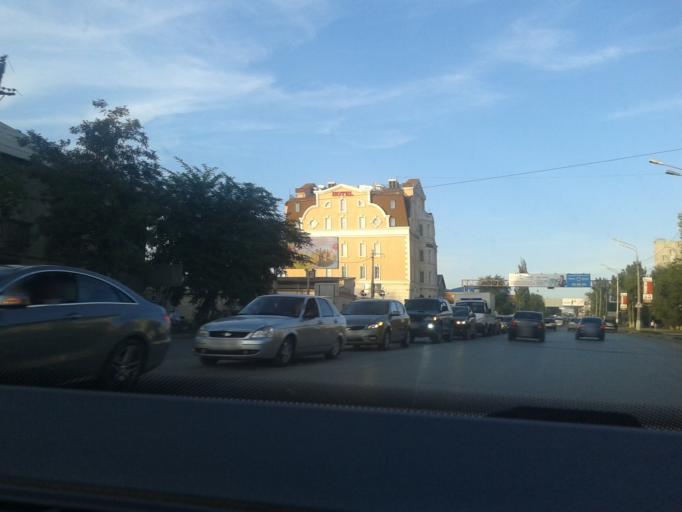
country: RU
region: Volgograd
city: Volgograd
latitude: 48.7140
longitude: 44.4981
